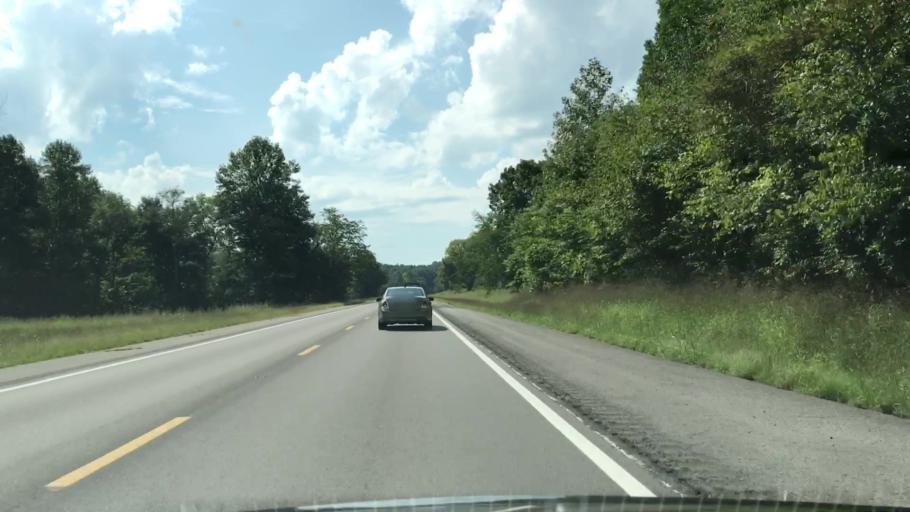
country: US
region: Tennessee
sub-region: Sumner County
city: Westmoreland
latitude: 36.6131
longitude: -86.2341
